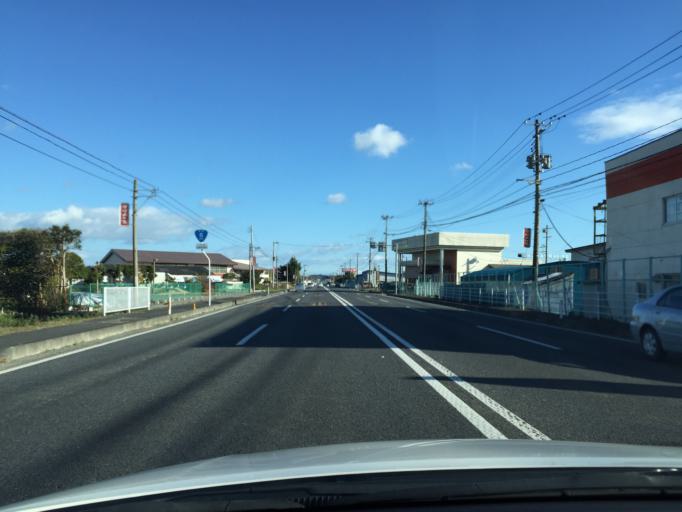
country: JP
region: Fukushima
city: Iwaki
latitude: 37.0840
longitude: 140.9653
